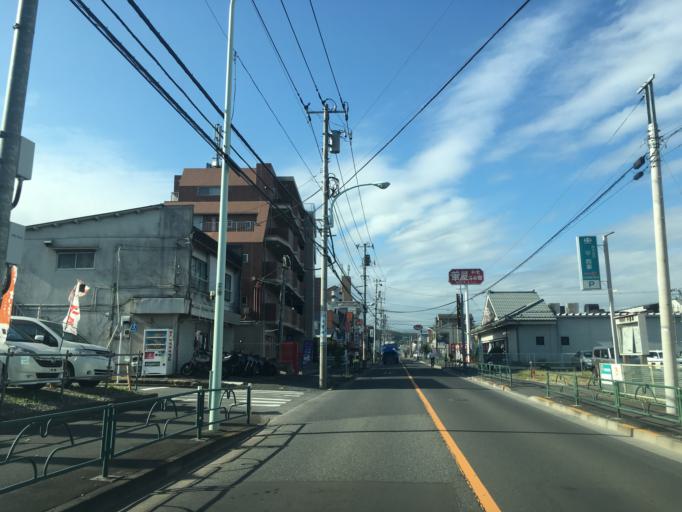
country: JP
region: Tokyo
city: Hino
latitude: 35.6563
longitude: 139.3962
